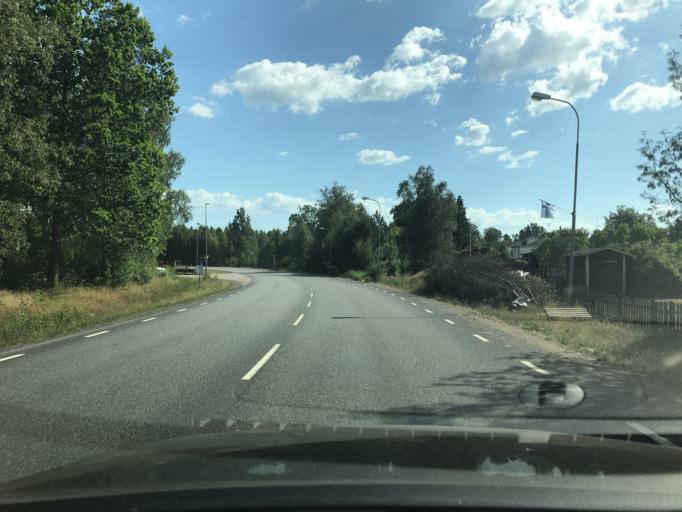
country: SE
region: Skane
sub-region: Hassleholms Kommun
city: Hastveda
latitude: 56.2813
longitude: 13.9332
